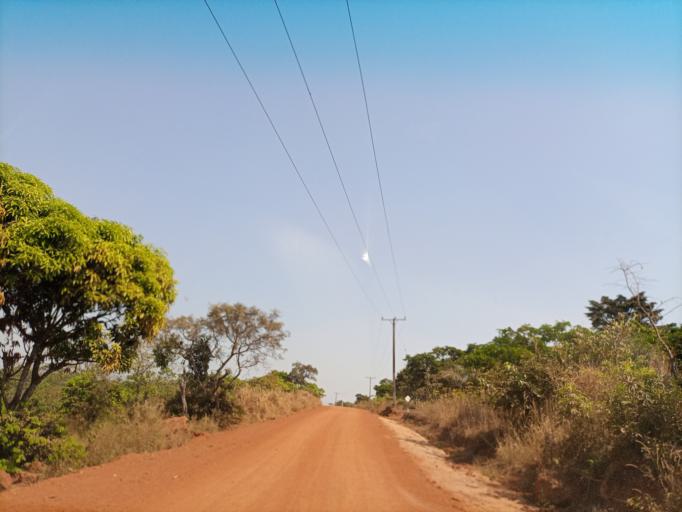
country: NG
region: Enugu
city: Nsukka
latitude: 6.7996
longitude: 7.3446
